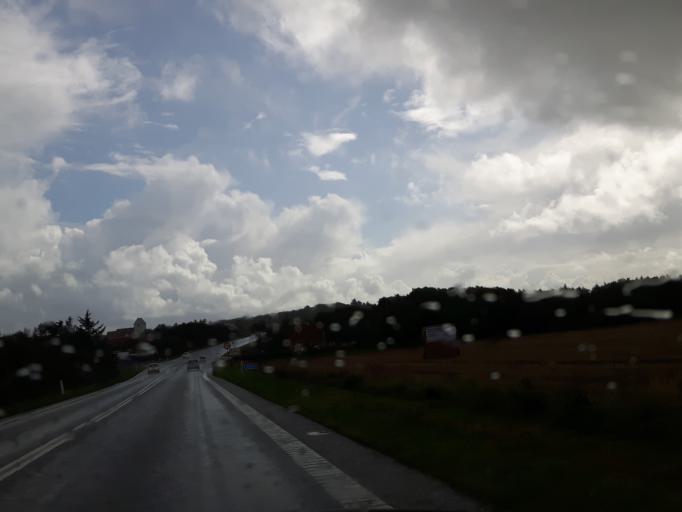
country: DK
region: Central Jutland
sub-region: Struer Kommune
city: Struer
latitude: 56.6100
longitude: 8.5282
